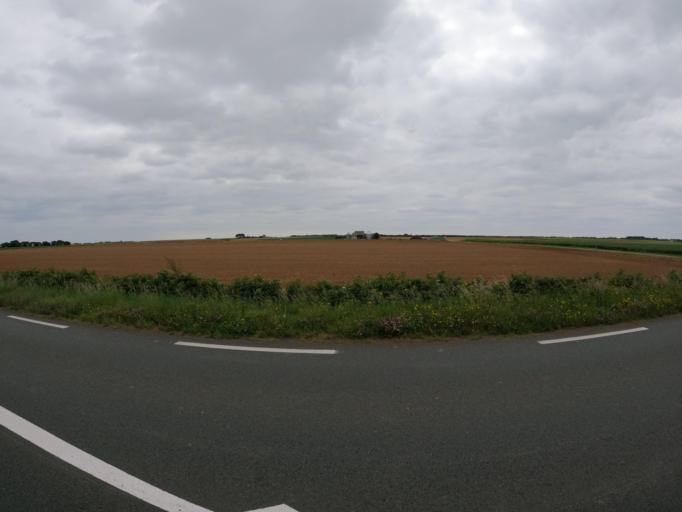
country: FR
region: Pays de la Loire
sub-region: Departement de la Vendee
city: Sainte-Hermine
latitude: 46.5463
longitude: -1.0350
